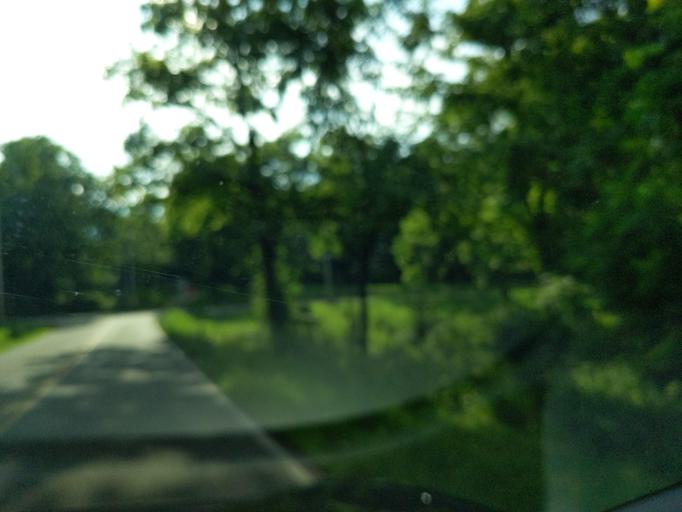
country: US
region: Ohio
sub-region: Fairfield County
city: Lancaster
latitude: 39.5519
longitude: -82.6380
